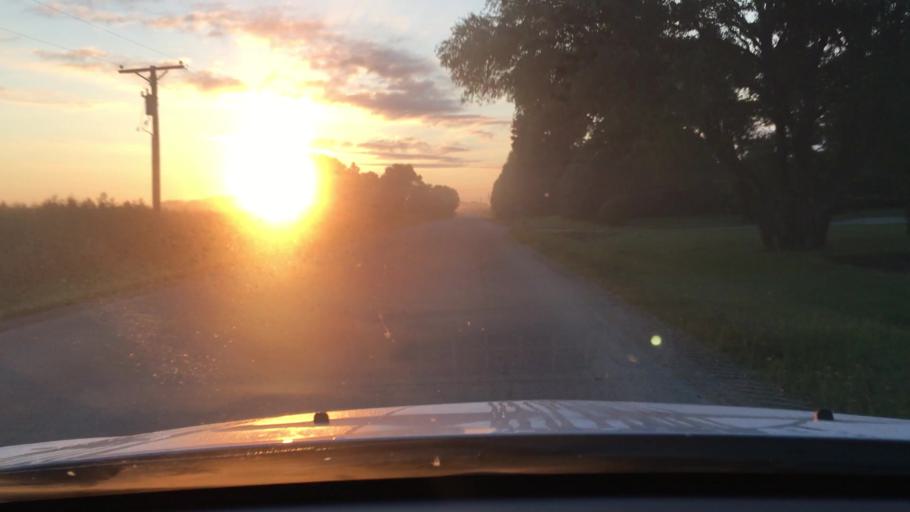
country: US
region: Illinois
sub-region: DeKalb County
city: Malta
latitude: 41.8486
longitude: -88.8770
